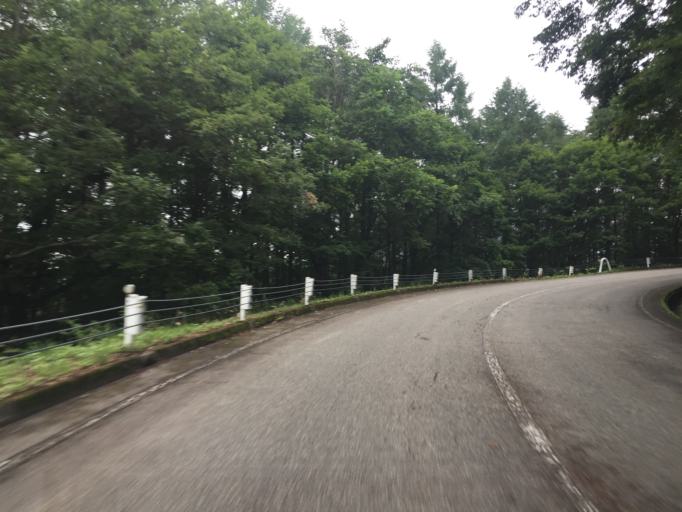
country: JP
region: Fukushima
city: Inawashiro
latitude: 37.6685
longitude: 140.1027
